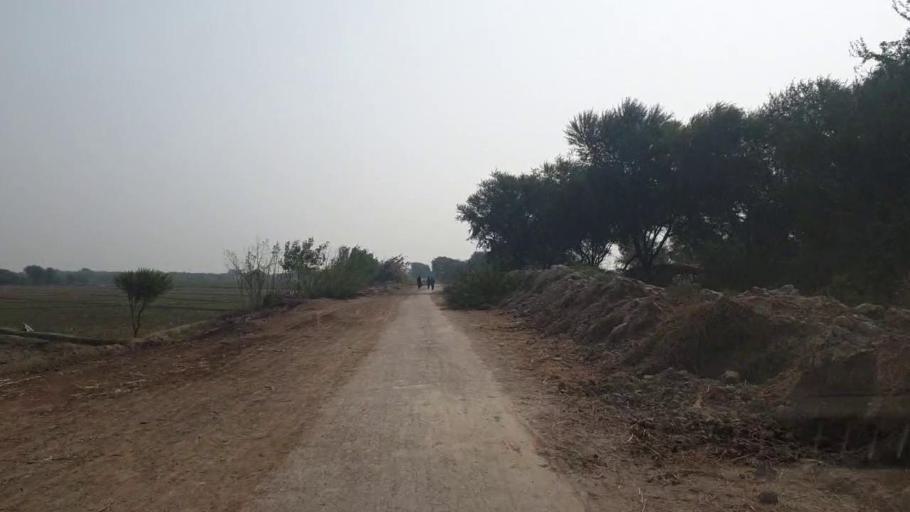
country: PK
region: Sindh
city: Tando Muhammad Khan
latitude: 25.2707
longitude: 68.4968
